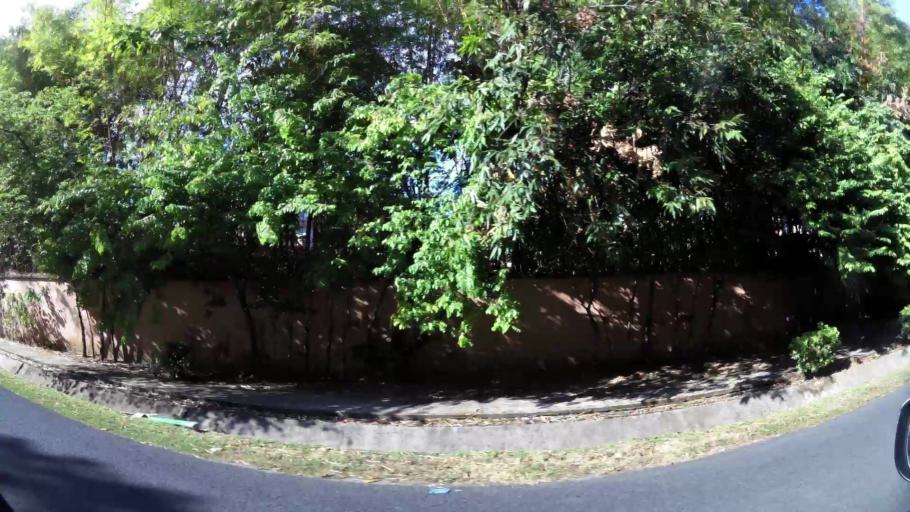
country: CR
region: Puntarenas
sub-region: Canton de Garabito
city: Jaco
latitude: 9.6485
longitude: -84.6555
